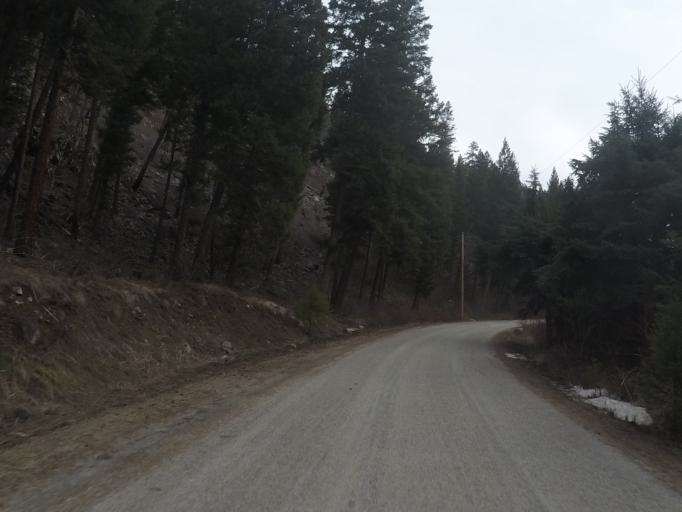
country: US
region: Montana
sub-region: Ravalli County
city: Hamilton
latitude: 45.8478
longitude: -114.0341
